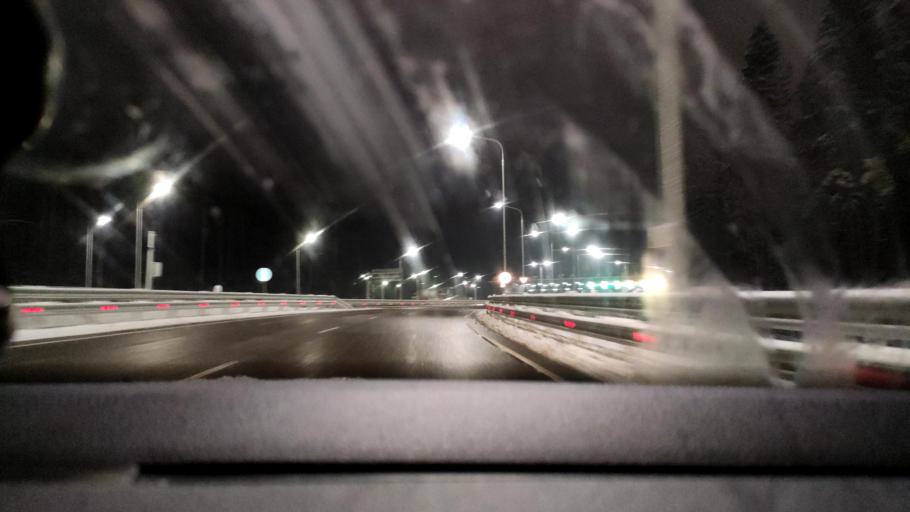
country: RU
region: Moskovskaya
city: Solnechnogorsk
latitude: 56.1585
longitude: 36.9132
